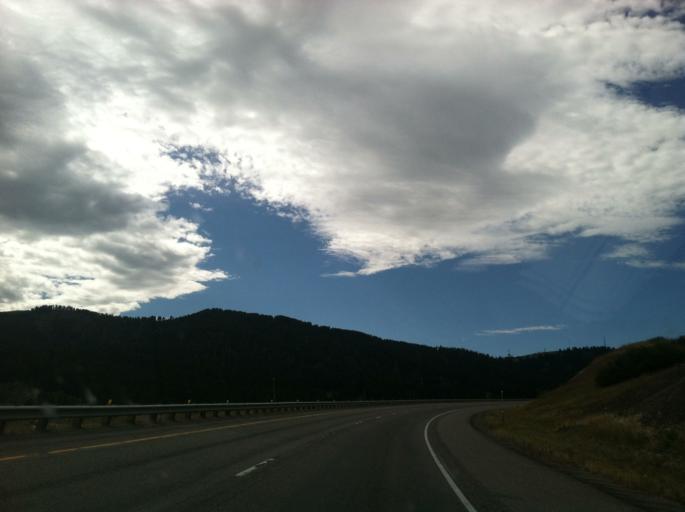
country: US
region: Montana
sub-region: Park County
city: Livingston
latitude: 45.6562
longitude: -110.7742
